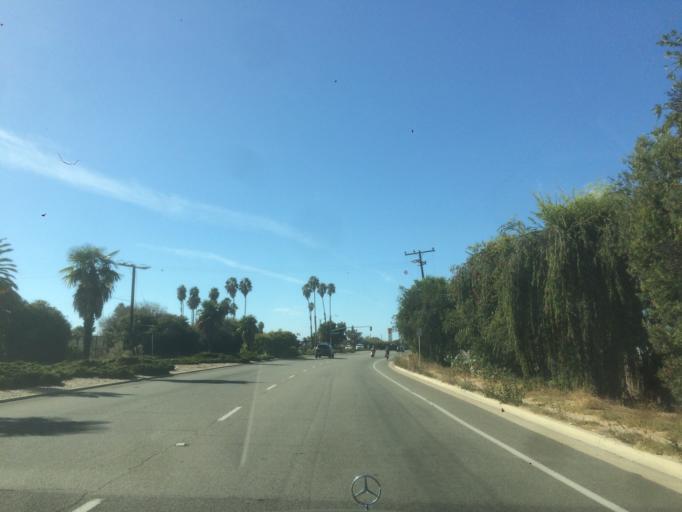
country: US
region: California
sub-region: Santa Barbara County
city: Goleta
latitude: 34.4351
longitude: -119.8332
